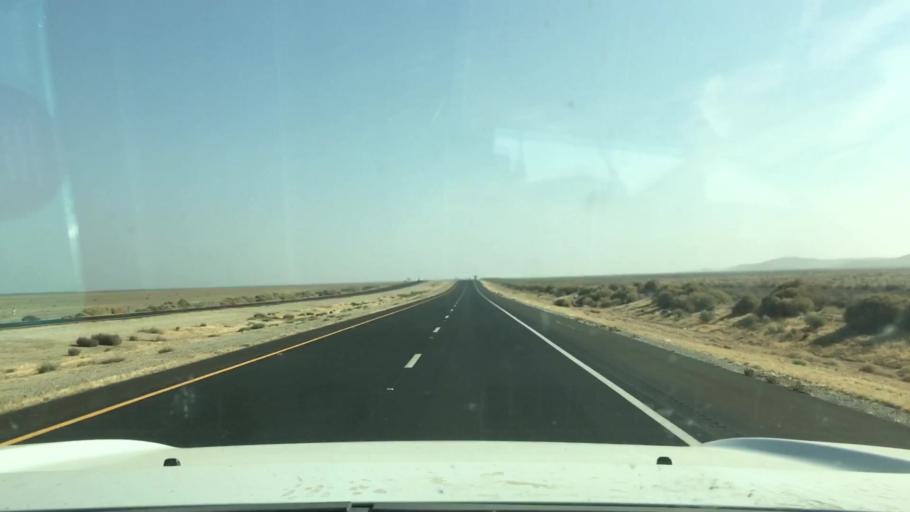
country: US
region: California
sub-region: Kern County
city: Lost Hills
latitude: 35.6365
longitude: -120.0108
